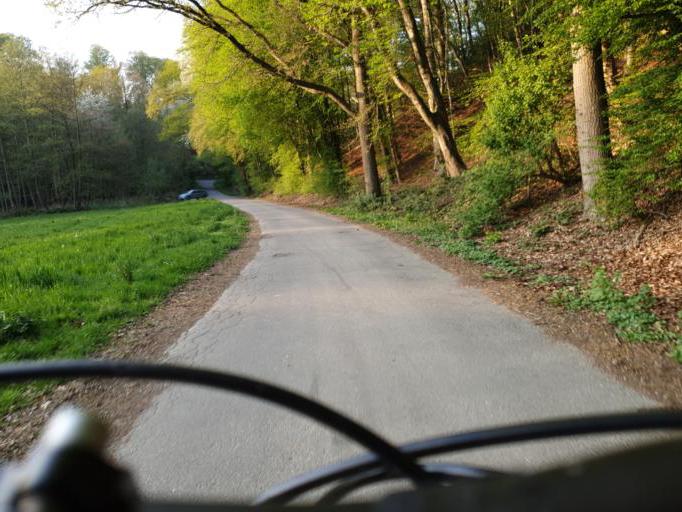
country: DE
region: North Rhine-Westphalia
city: Burscheid
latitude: 51.0692
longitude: 7.0743
